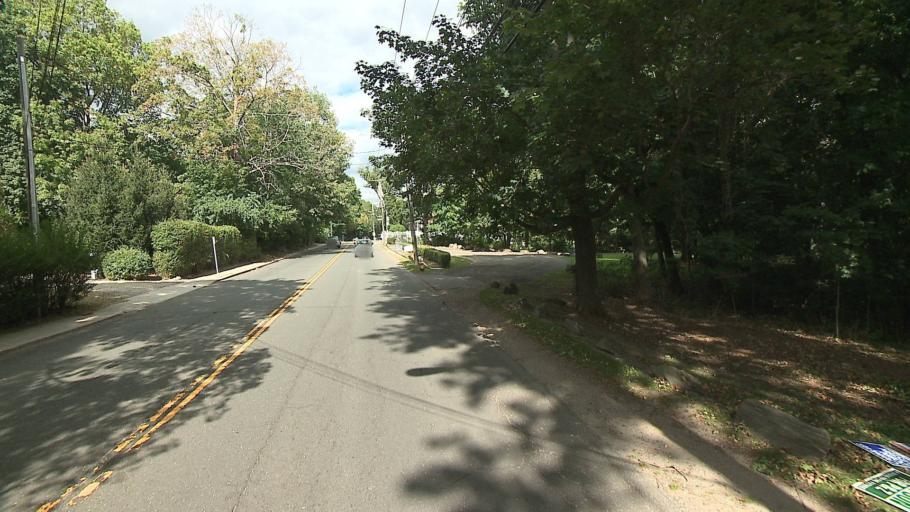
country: US
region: Connecticut
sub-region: Fairfield County
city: Westport
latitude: 41.1265
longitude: -73.3714
